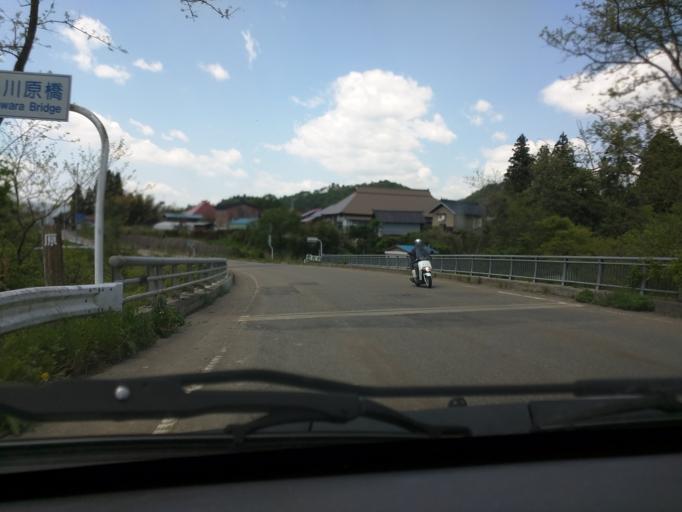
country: JP
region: Fukushima
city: Kitakata
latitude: 37.6410
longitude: 139.7913
